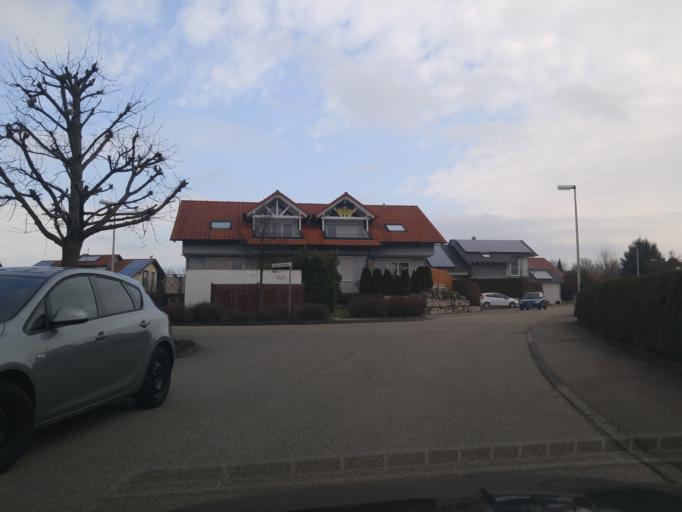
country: DE
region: Baden-Wuerttemberg
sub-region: Regierungsbezirk Stuttgart
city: Ilsfeld
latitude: 49.0570
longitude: 9.2387
